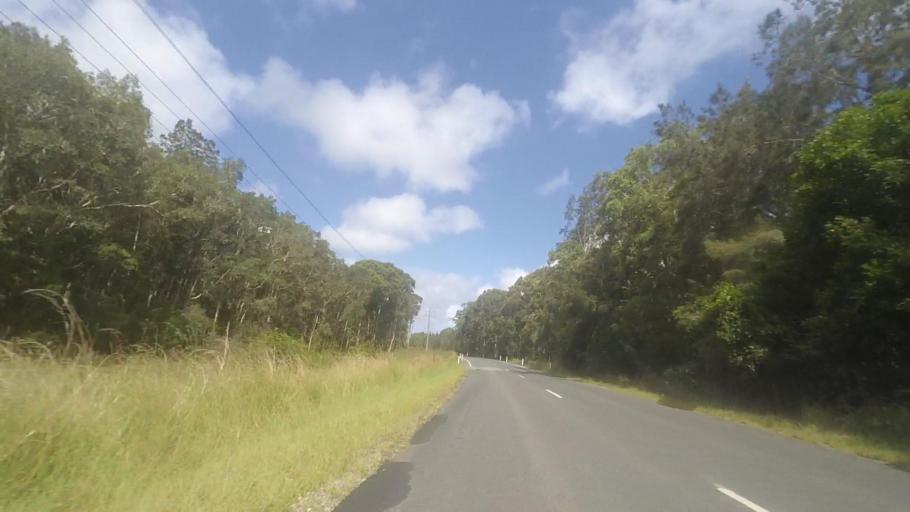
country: AU
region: New South Wales
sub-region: Great Lakes
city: Bulahdelah
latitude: -32.3842
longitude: 152.3971
